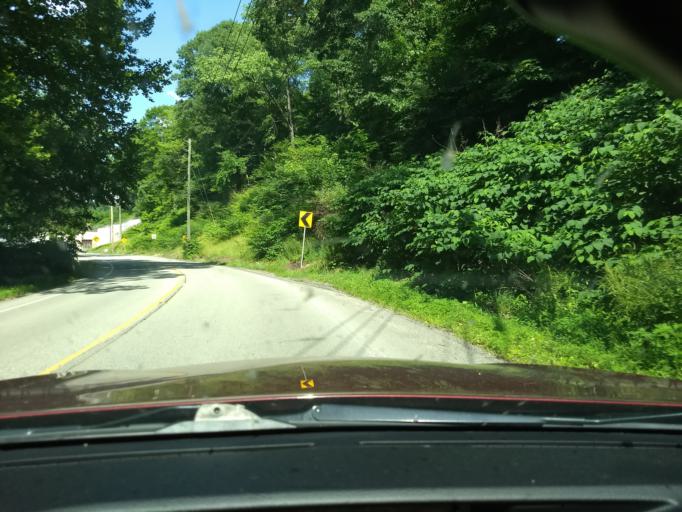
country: US
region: Pennsylvania
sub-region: Westmoreland County
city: Irwin
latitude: 40.3388
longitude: -79.7233
